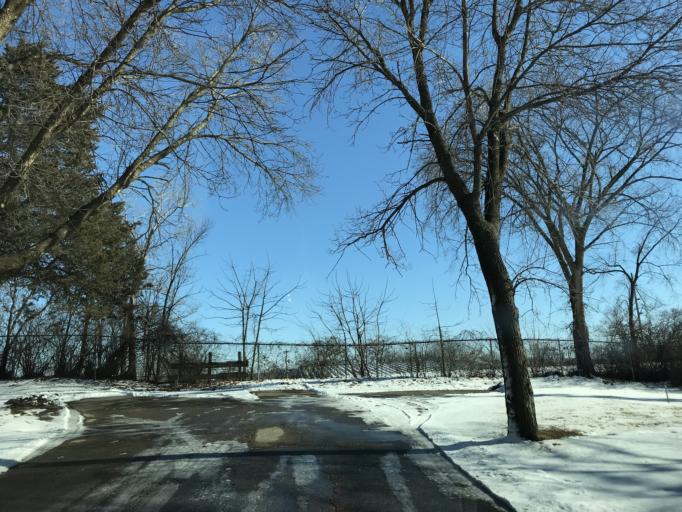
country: US
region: Wisconsin
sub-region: Dane County
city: Monona
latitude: 43.0488
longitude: -89.3182
